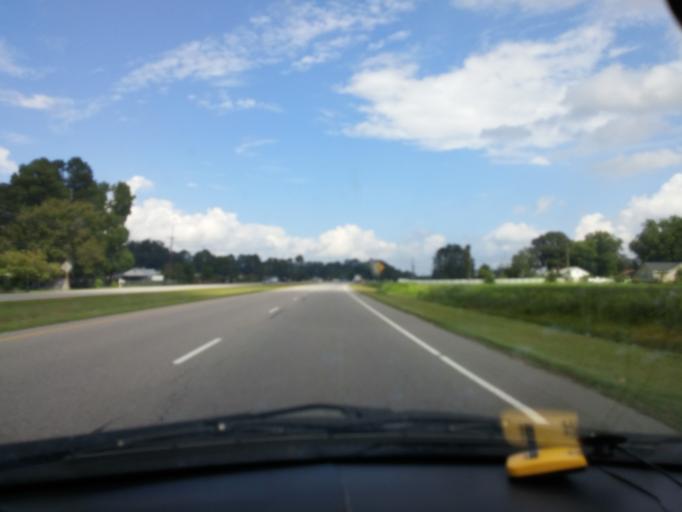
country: US
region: North Carolina
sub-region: Pitt County
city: Grifton
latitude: 35.3580
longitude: -77.4644
